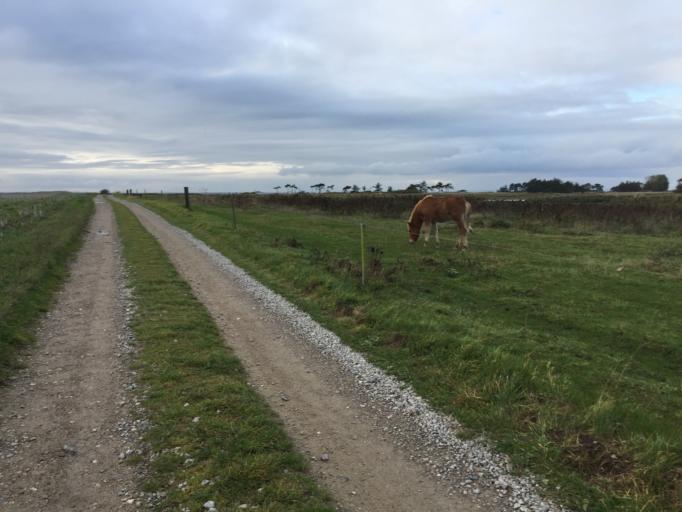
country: DK
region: Zealand
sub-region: Slagelse Kommune
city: Skaelskor
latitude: 55.2069
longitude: 11.1791
